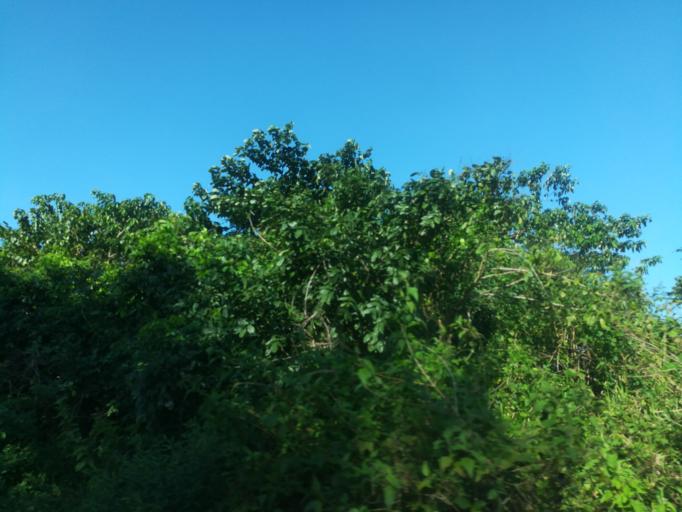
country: NG
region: Lagos
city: Ikorodu
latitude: 6.5623
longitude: 3.5350
